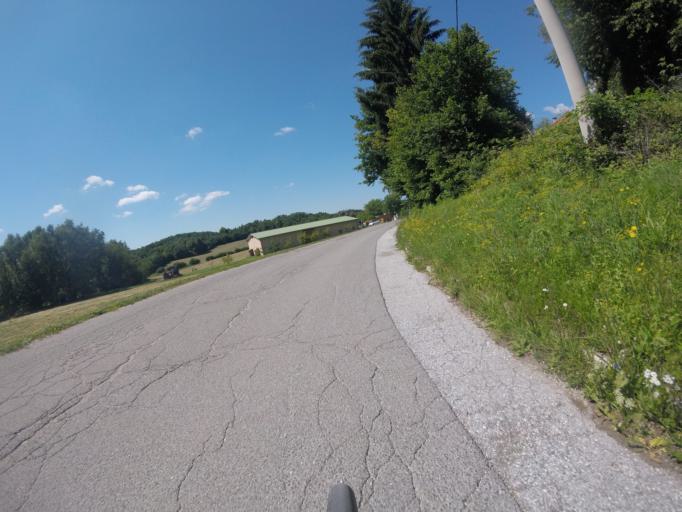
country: SI
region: Kostanjevica na Krki
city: Kostanjevica na Krki
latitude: 45.7917
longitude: 15.4938
